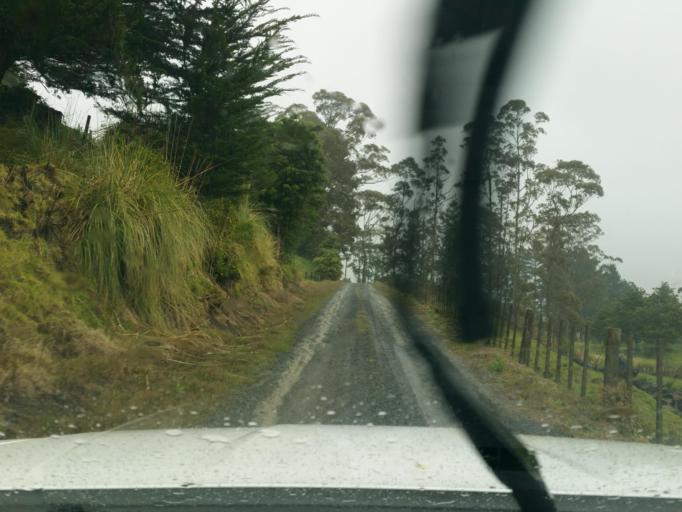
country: NZ
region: Northland
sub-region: Kaipara District
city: Dargaville
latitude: -35.8641
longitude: 174.0187
